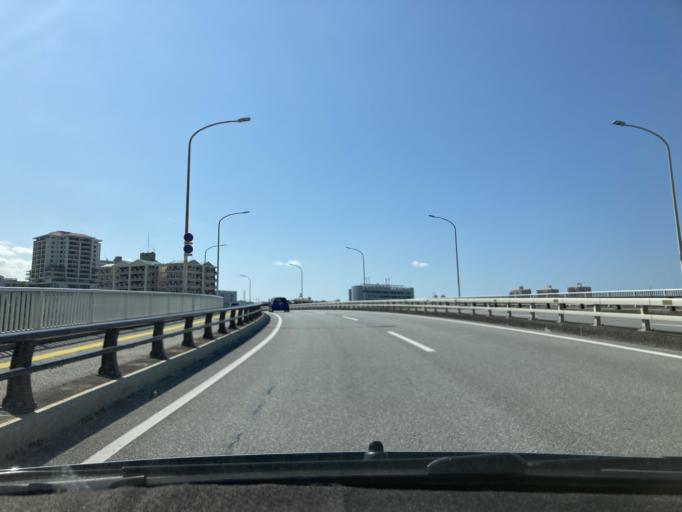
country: JP
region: Okinawa
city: Ginowan
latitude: 26.2715
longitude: 127.7262
